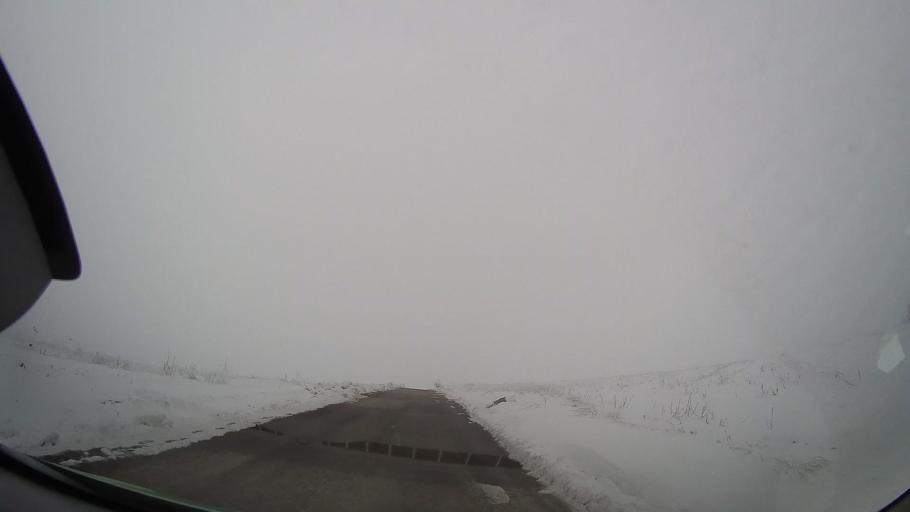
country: RO
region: Iasi
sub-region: Comuna Dagata
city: Dagata
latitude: 46.9070
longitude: 27.1968
